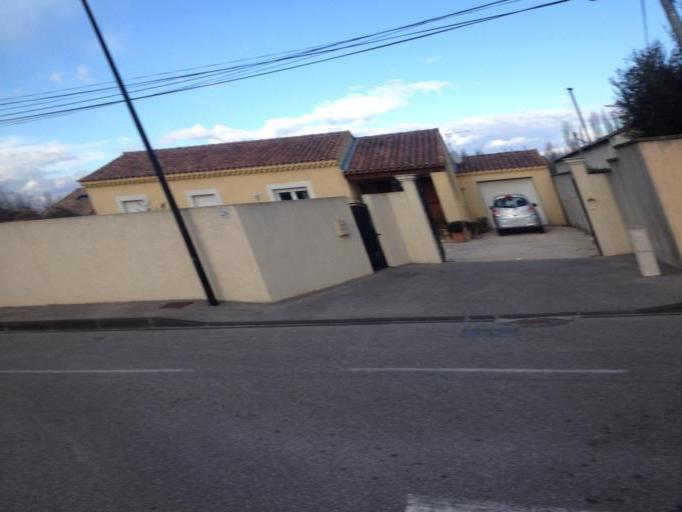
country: FR
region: Provence-Alpes-Cote d'Azur
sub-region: Departement du Vaucluse
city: Orange
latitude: 44.1225
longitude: 4.8328
